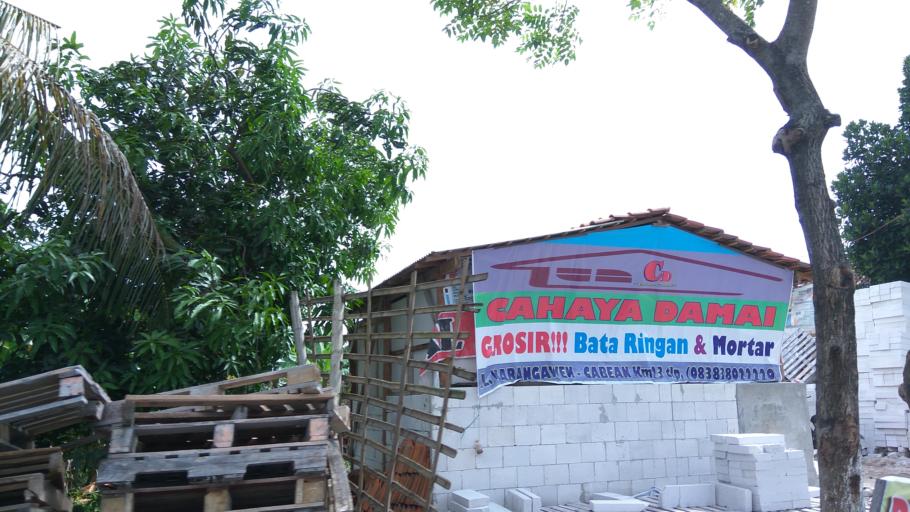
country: ID
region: Central Java
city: Mranggen
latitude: -7.0484
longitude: 110.5933
